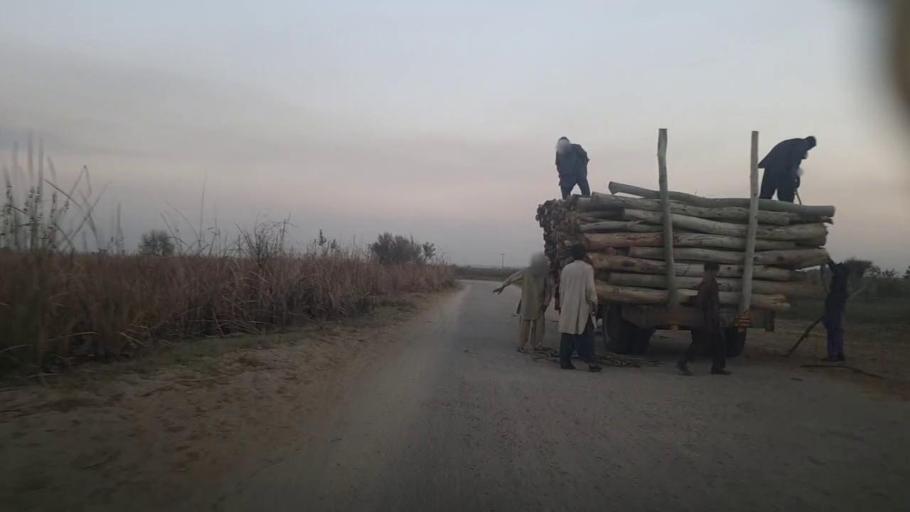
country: PK
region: Sindh
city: Kandiari
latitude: 26.6782
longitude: 68.9445
